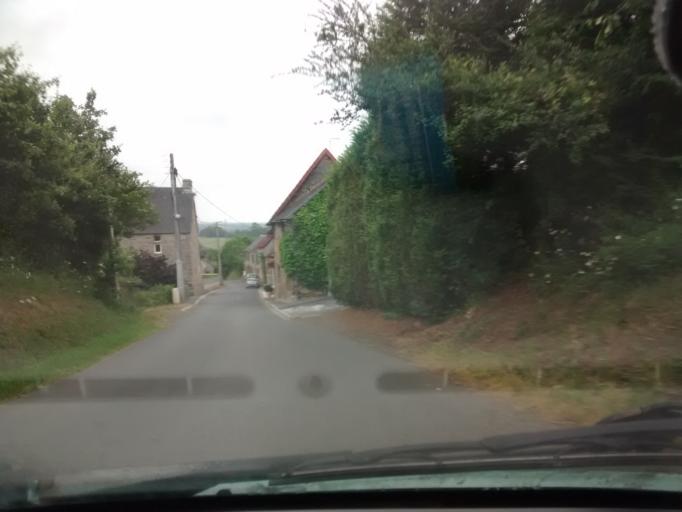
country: FR
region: Lower Normandy
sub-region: Departement de la Manche
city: Saint-Lo
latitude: 49.0977
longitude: -1.0791
